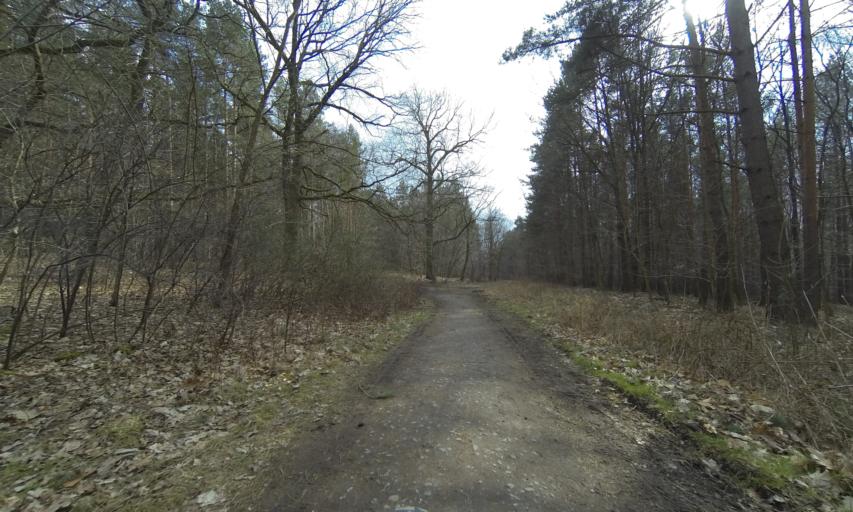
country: DE
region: Saxony
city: Albertstadt
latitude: 51.1057
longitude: 13.7160
